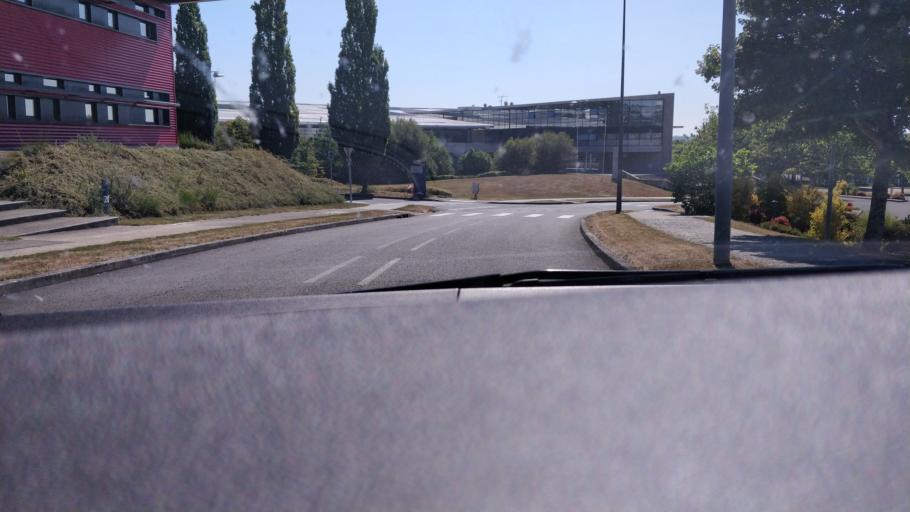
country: FR
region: Limousin
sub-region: Departement de la Haute-Vienne
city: Le Palais-sur-Vienne
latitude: 45.8619
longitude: 1.2938
